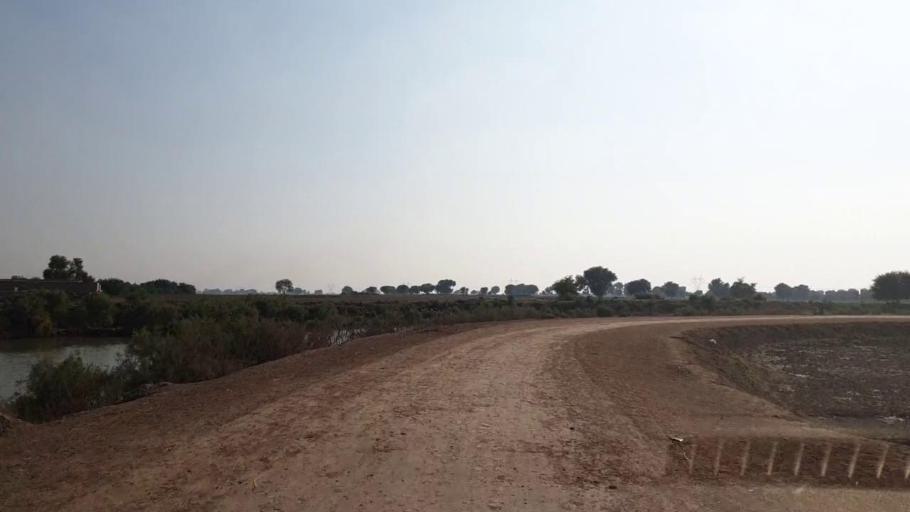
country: PK
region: Sindh
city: Sehwan
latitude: 26.4403
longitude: 67.8072
